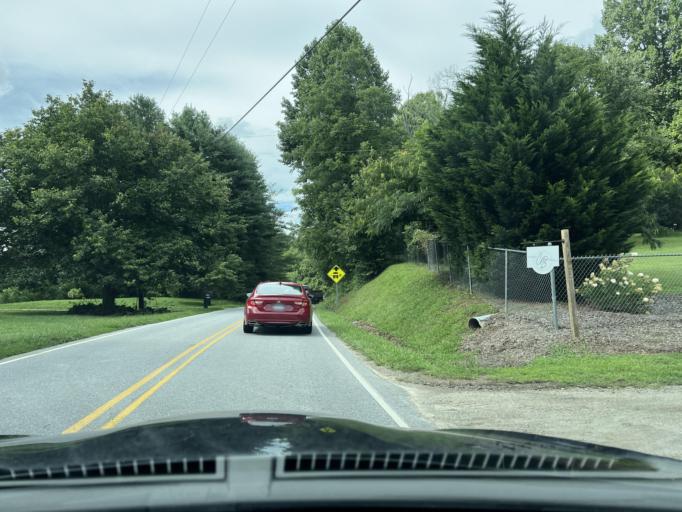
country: US
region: North Carolina
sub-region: Henderson County
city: Hoopers Creek
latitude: 35.4340
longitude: -82.4292
